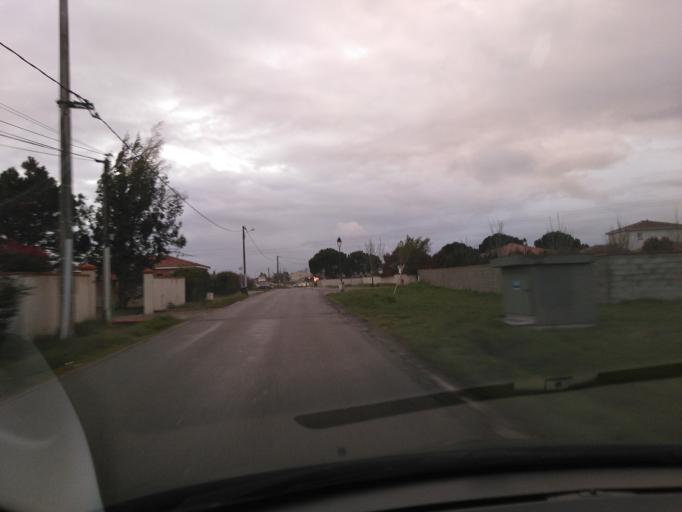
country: FR
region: Midi-Pyrenees
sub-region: Departement de la Haute-Garonne
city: Beauzelle
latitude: 43.6748
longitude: 1.3591
